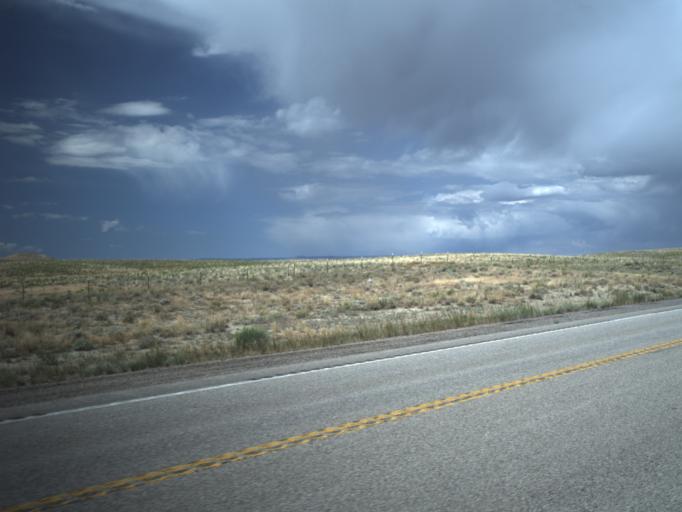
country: US
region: Utah
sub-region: Carbon County
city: Wellington
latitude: 39.5325
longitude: -110.5889
